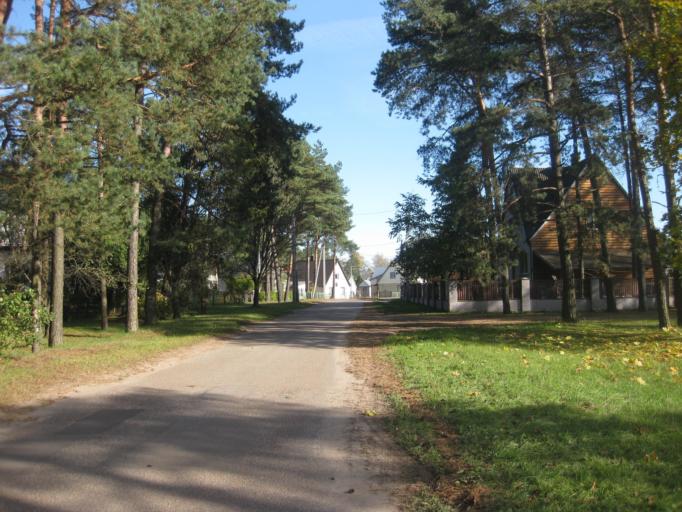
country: LT
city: Ezerelis
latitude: 54.8846
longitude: 23.5929
